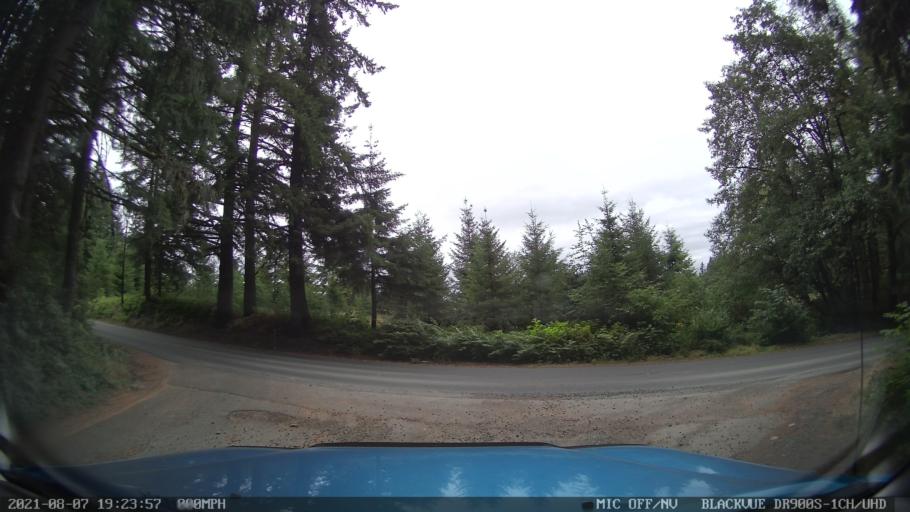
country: US
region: Oregon
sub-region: Linn County
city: Lyons
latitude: 44.8532
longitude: -122.6599
